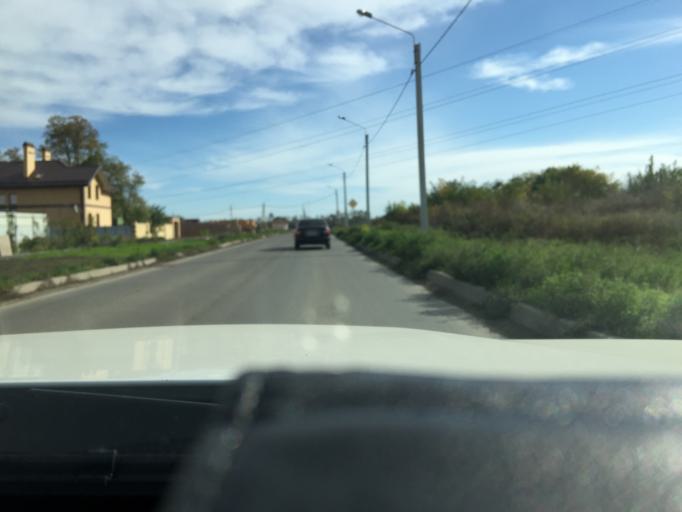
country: RU
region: Rostov
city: Imeni Chkalova
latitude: 47.2981
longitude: 39.8119
